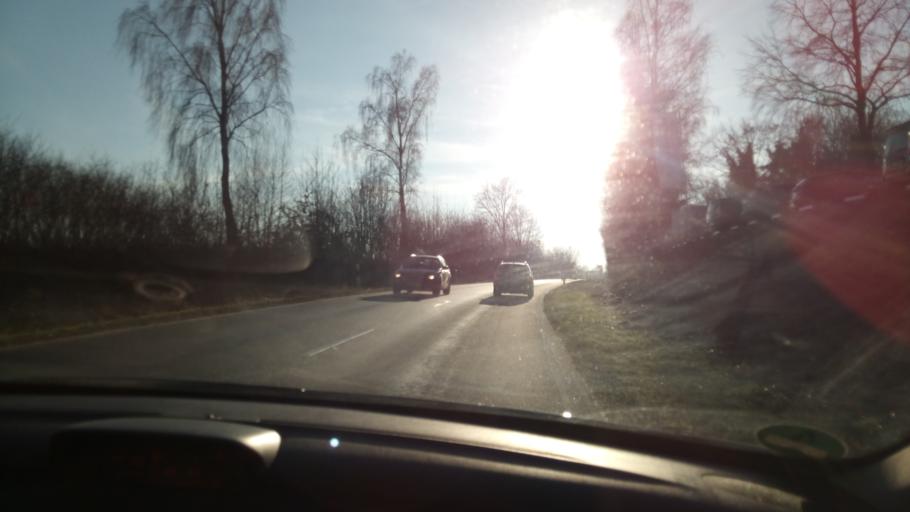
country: DE
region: Schleswig-Holstein
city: Buchhorst
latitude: 53.3891
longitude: 10.5564
